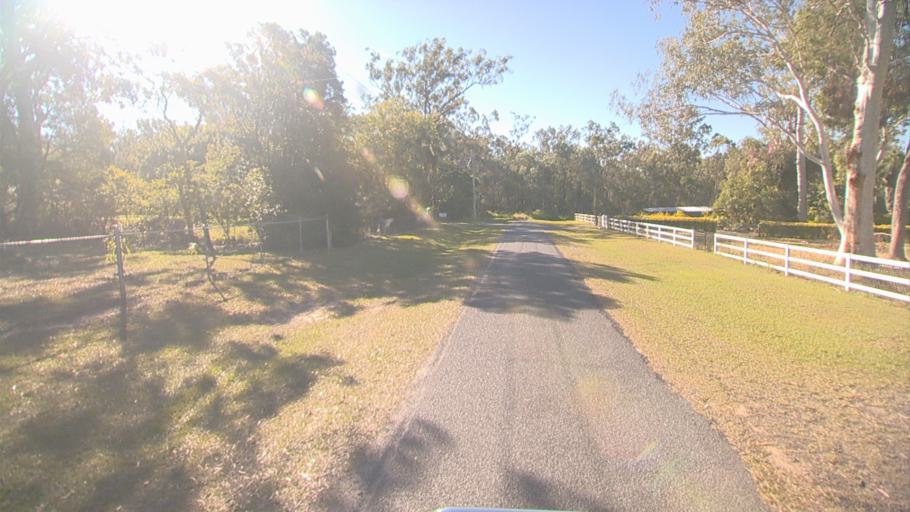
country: AU
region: Queensland
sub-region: Logan
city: Logan Reserve
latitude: -27.7290
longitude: 153.0785
